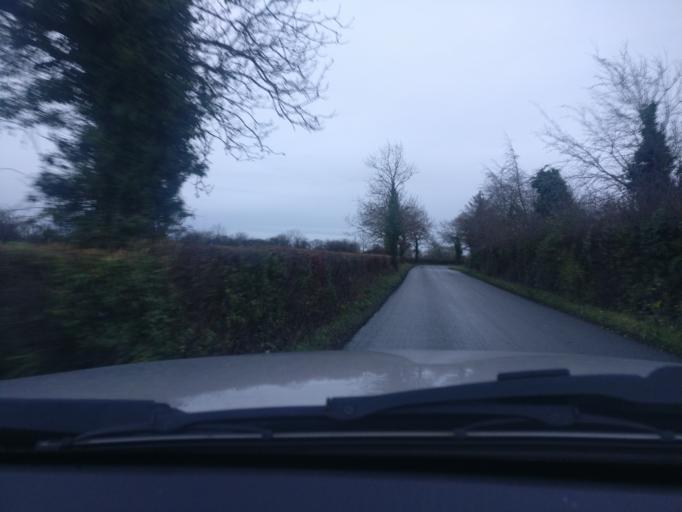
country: IE
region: Leinster
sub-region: Kildare
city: Maynooth
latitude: 53.4161
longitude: -6.6113
